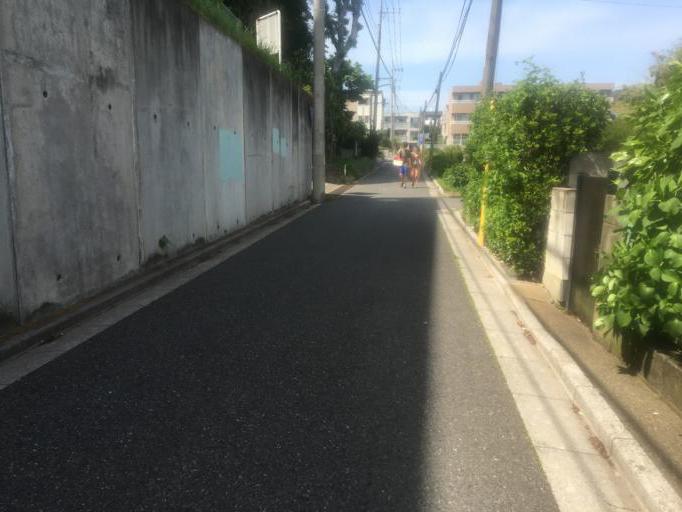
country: JP
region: Saitama
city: Yono
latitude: 35.8493
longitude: 139.6539
